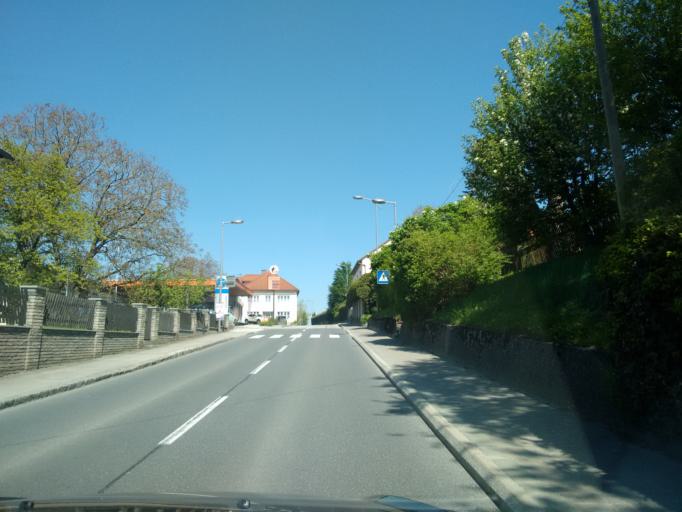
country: AT
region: Upper Austria
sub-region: Politischer Bezirk Steyr-Land
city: Waldneukirchen
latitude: 47.9984
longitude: 14.2601
